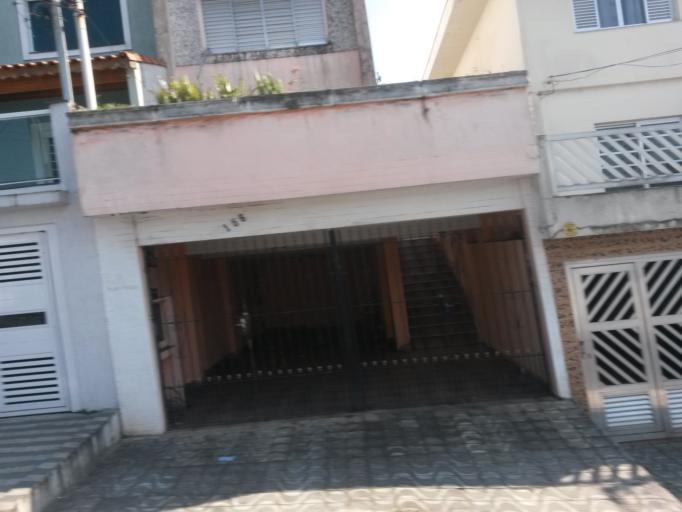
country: BR
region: Sao Paulo
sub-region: Sao Bernardo Do Campo
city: Sao Bernardo do Campo
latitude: -23.7014
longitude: -46.5645
